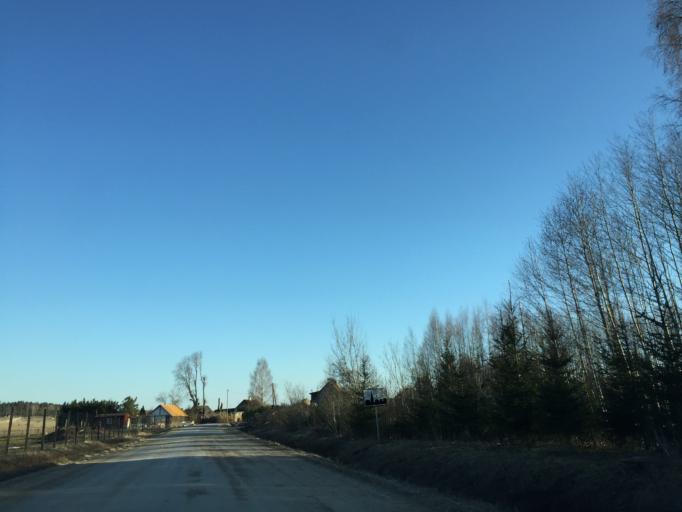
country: EE
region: Ida-Virumaa
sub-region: Sillamaee linn
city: Sillamae
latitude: 59.1264
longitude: 27.8028
